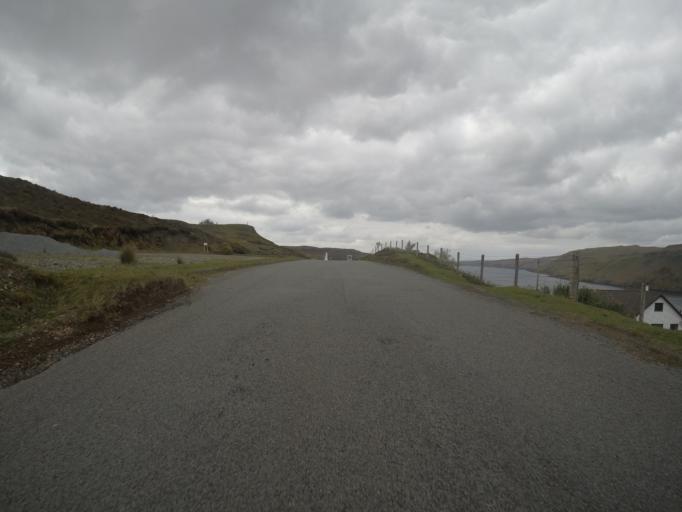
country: GB
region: Scotland
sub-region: Highland
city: Isle of Skye
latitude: 57.2957
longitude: -6.3393
